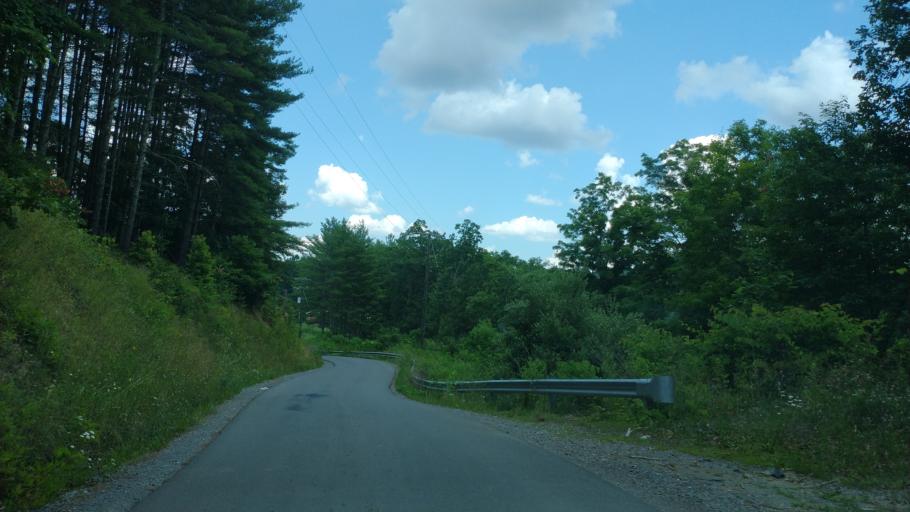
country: US
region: West Virginia
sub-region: Mercer County
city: Athens
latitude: 37.4654
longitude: -81.0659
